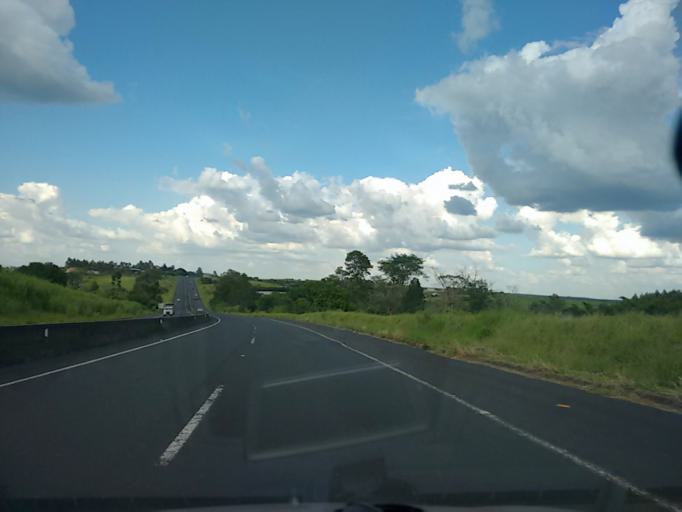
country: BR
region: Sao Paulo
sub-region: Marilia
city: Marilia
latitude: -22.2327
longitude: -49.8122
